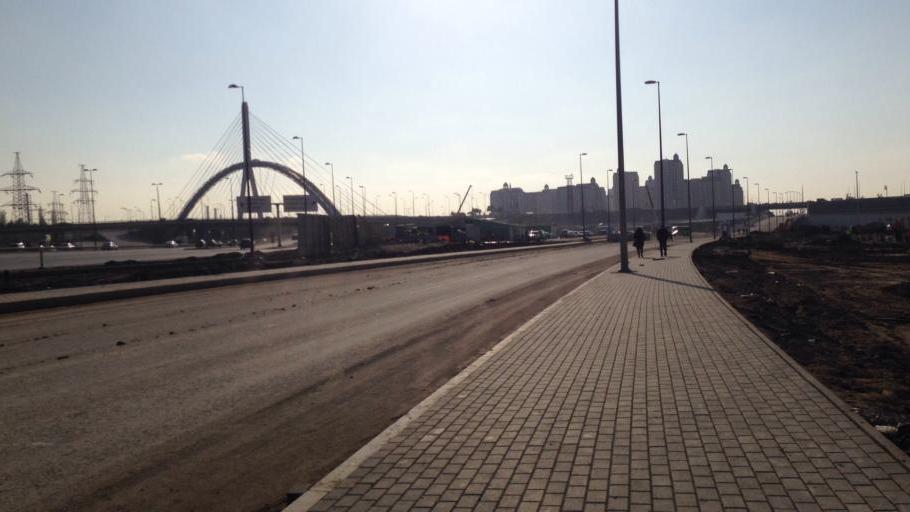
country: AZ
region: Baki
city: Sabuncu
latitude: 40.4281
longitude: 49.9232
